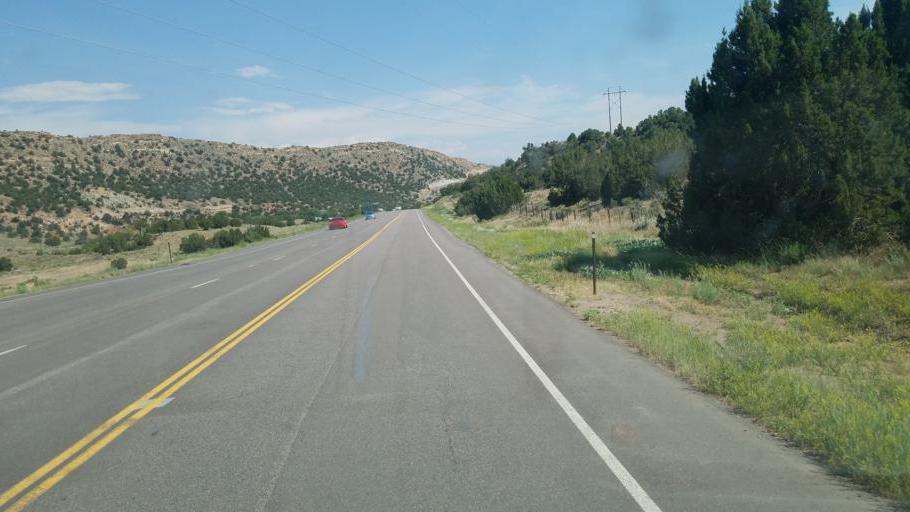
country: US
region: Colorado
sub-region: Fremont County
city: Canon City
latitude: 38.4794
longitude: -105.2637
